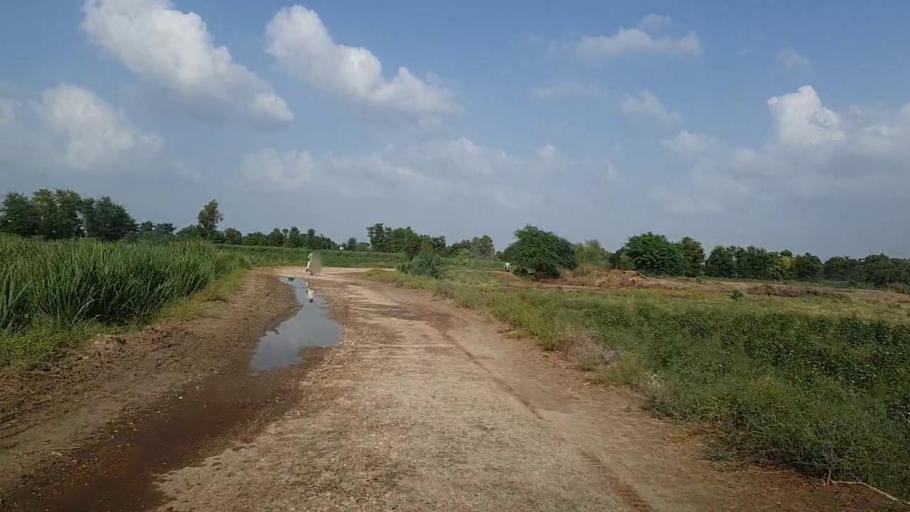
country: PK
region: Sindh
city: Bhiria
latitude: 26.8474
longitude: 68.2384
